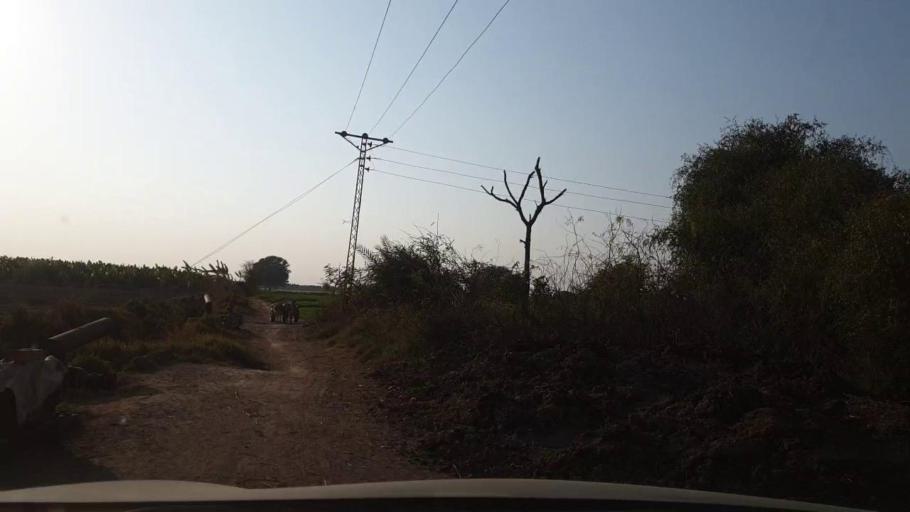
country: PK
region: Sindh
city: Tando Allahyar
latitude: 25.5745
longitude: 68.7920
